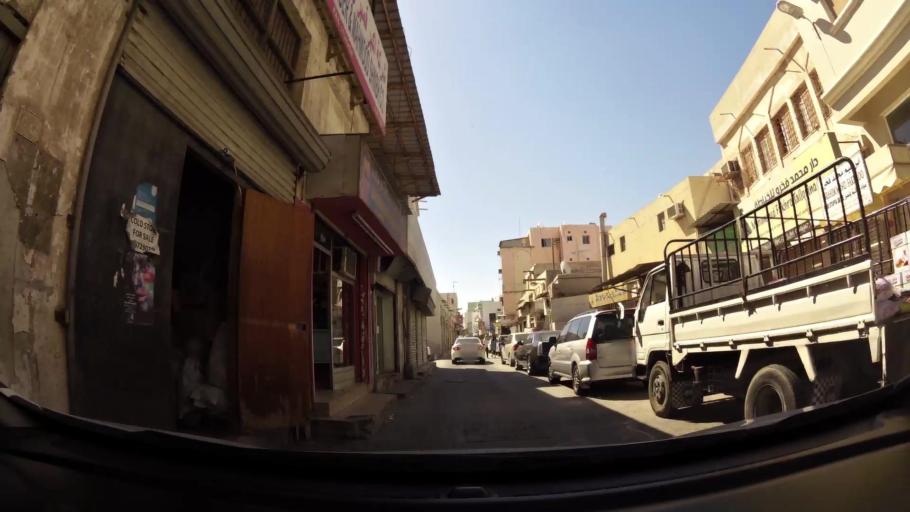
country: BH
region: Muharraq
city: Al Muharraq
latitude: 26.2507
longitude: 50.6098
